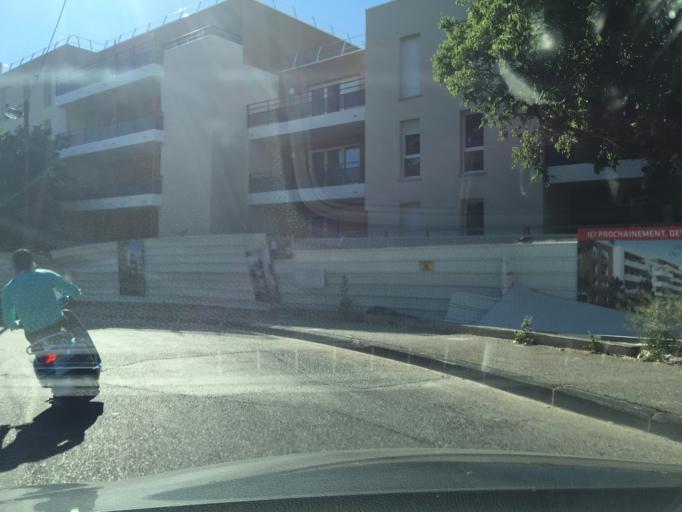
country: FR
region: Provence-Alpes-Cote d'Azur
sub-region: Departement des Bouches-du-Rhone
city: Marseille 09
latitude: 43.2340
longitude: 5.4074
